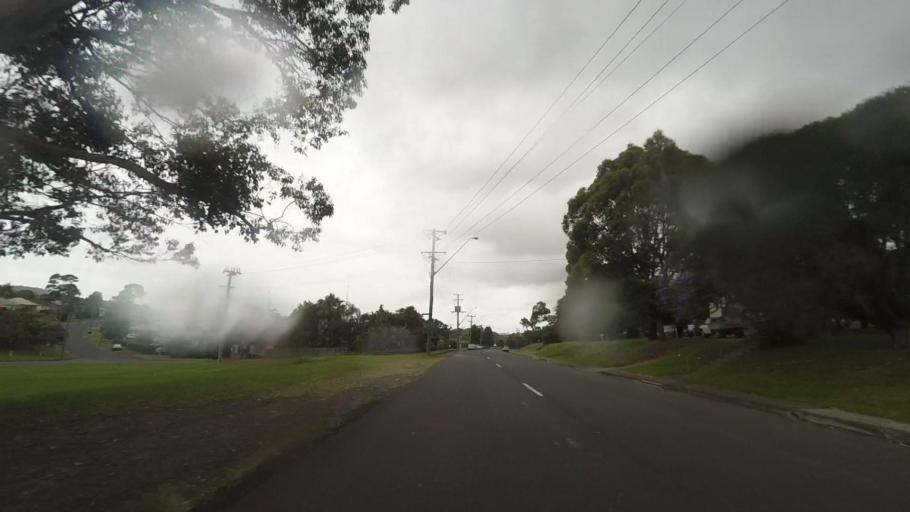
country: AU
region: New South Wales
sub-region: Wollongong
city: Cordeaux Heights
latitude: -34.4487
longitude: 150.8413
